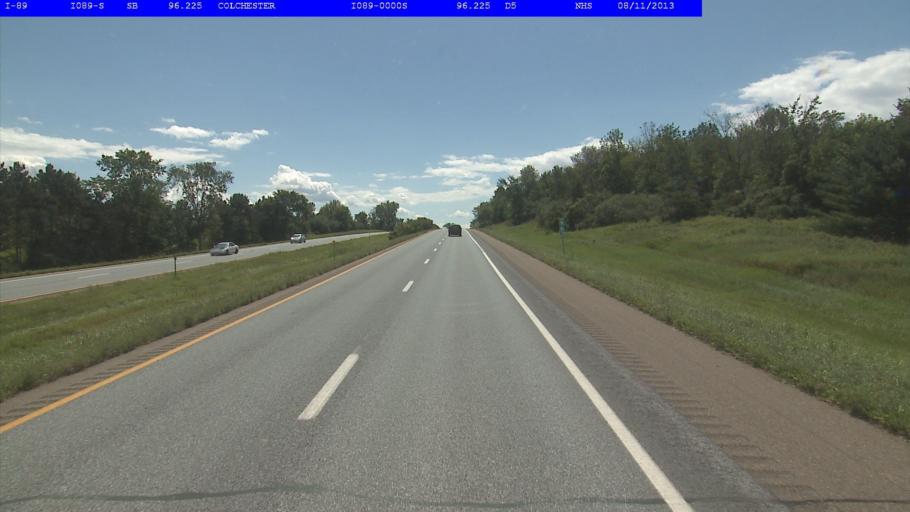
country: US
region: Vermont
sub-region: Chittenden County
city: Colchester
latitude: 44.5670
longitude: -73.1790
